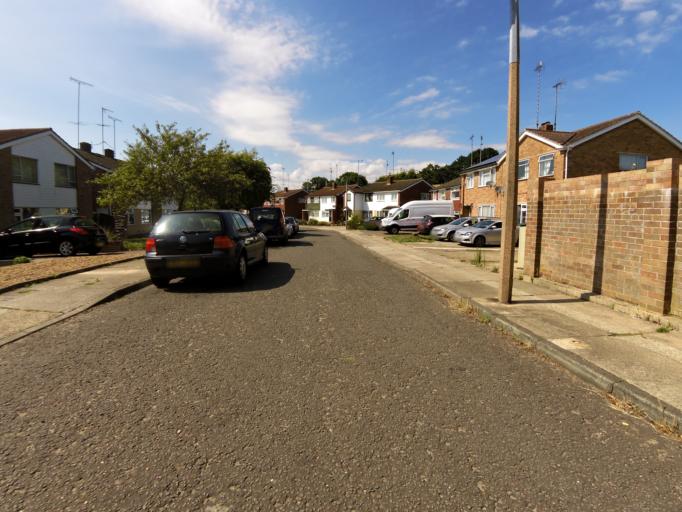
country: GB
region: England
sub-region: Essex
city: Colchester
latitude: 51.8983
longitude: 0.9162
